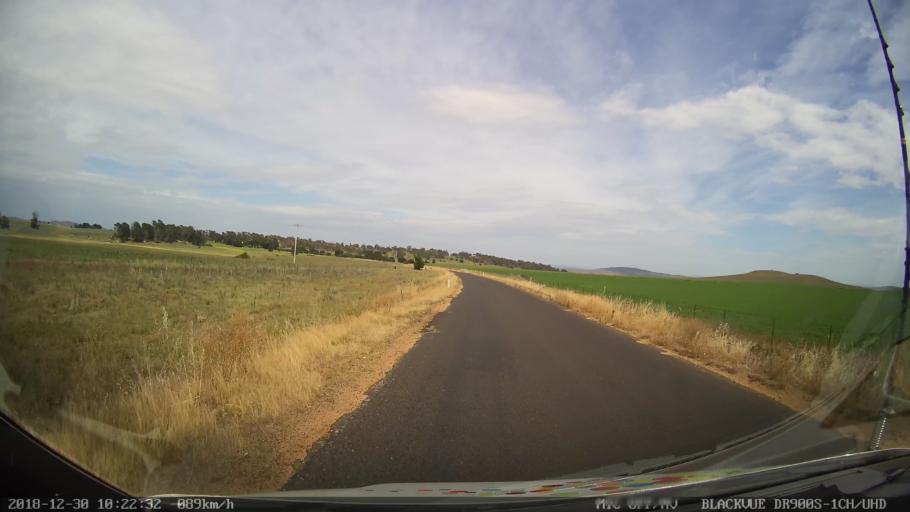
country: AU
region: New South Wales
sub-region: Snowy River
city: Berridale
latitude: -36.5433
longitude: 148.9937
